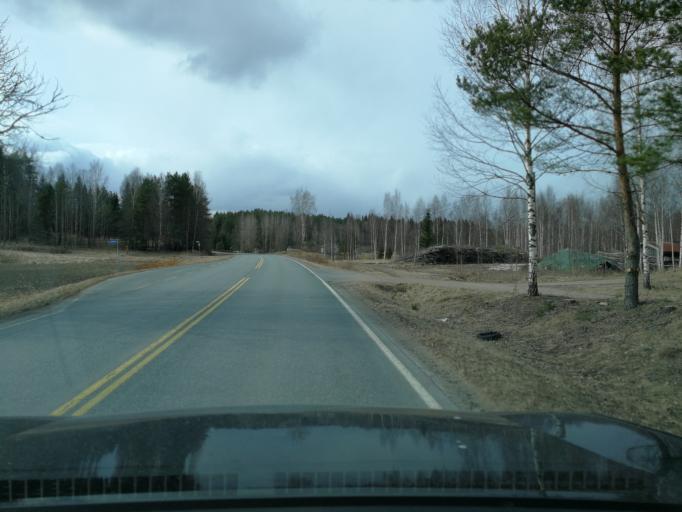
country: FI
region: Varsinais-Suomi
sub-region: Salo
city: Muurla
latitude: 60.2874
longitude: 23.3563
